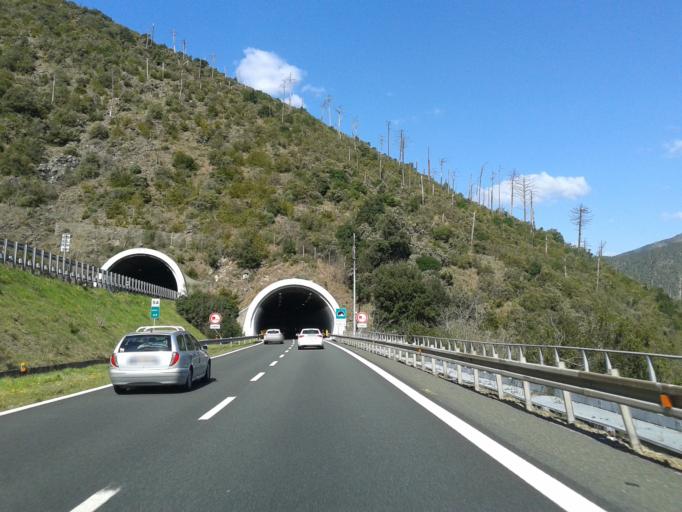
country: IT
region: Liguria
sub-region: Provincia di Genova
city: Moneglia
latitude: 44.2679
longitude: 9.4786
